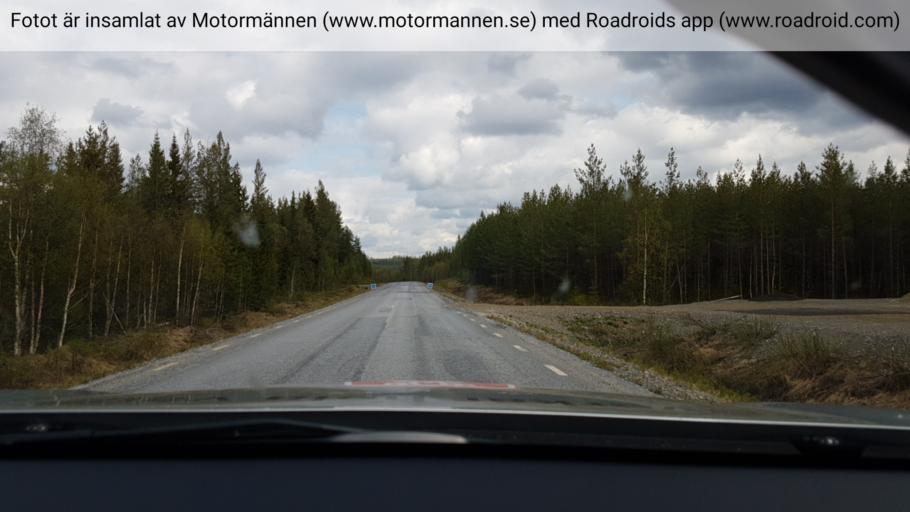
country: SE
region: Vaesternorrland
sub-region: OErnskoeldsviks Kommun
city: Bredbyn
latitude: 63.9619
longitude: 18.4969
